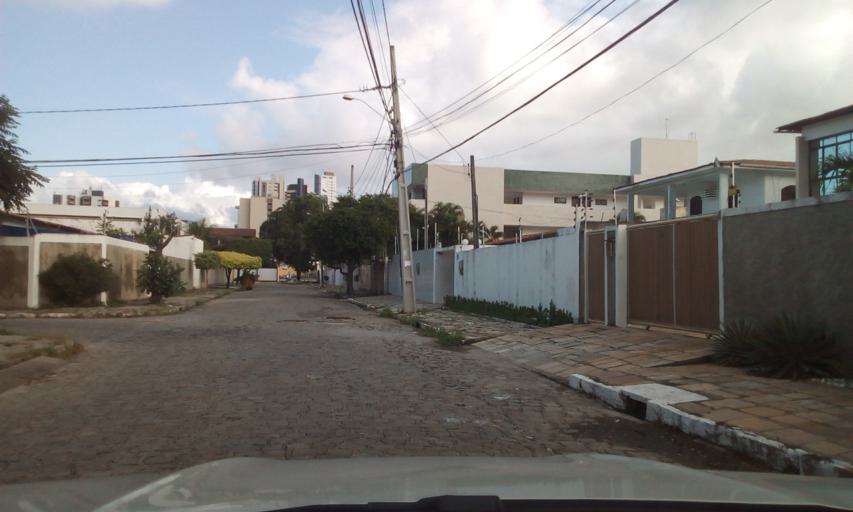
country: BR
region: Paraiba
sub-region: Joao Pessoa
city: Joao Pessoa
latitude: -7.0931
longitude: -34.8376
